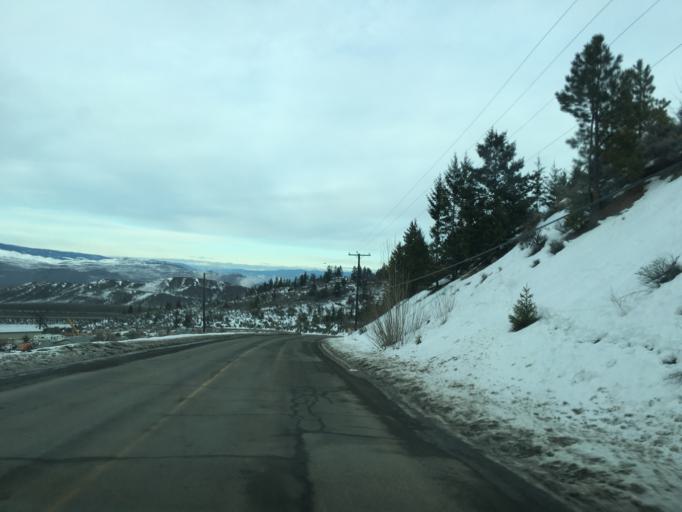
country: CA
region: British Columbia
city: Kamloops
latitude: 50.6567
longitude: -120.4373
